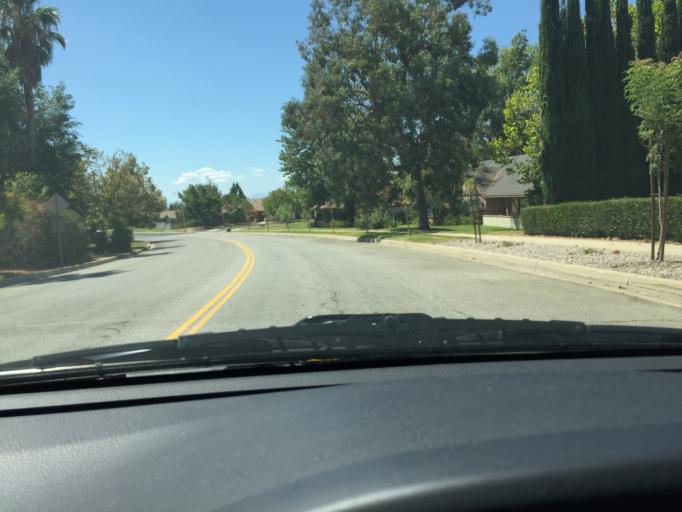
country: US
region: California
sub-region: San Bernardino County
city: Yucaipa
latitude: 34.0135
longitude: -117.0120
